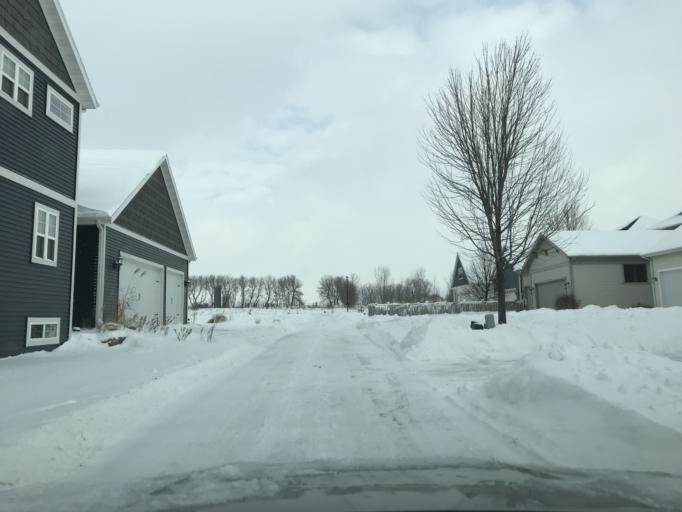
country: US
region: Wisconsin
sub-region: Dane County
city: Sun Prairie
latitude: 43.1668
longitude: -89.2832
